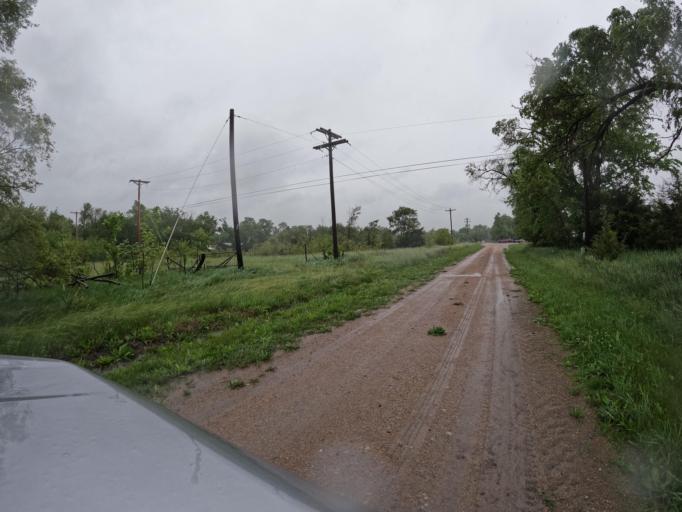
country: US
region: Nebraska
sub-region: Gage County
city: Wymore
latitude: 40.1427
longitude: -96.6684
